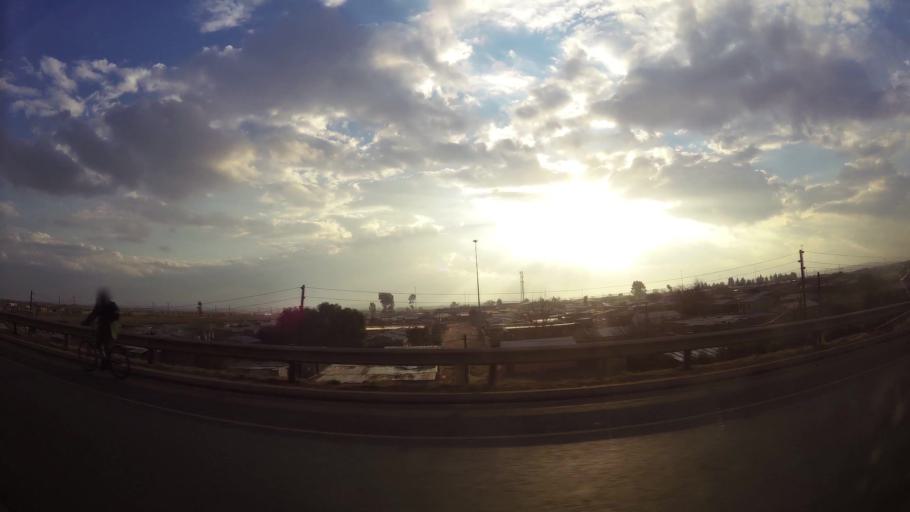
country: ZA
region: Gauteng
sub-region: Sedibeng District Municipality
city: Vanderbijlpark
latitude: -26.6050
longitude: 27.8171
